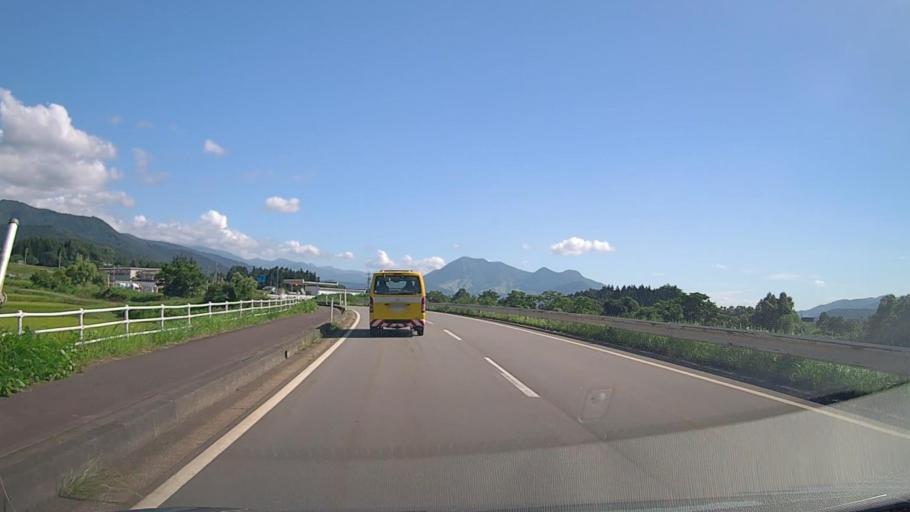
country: JP
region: Nagano
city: Iiyama
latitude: 36.9095
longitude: 138.3994
